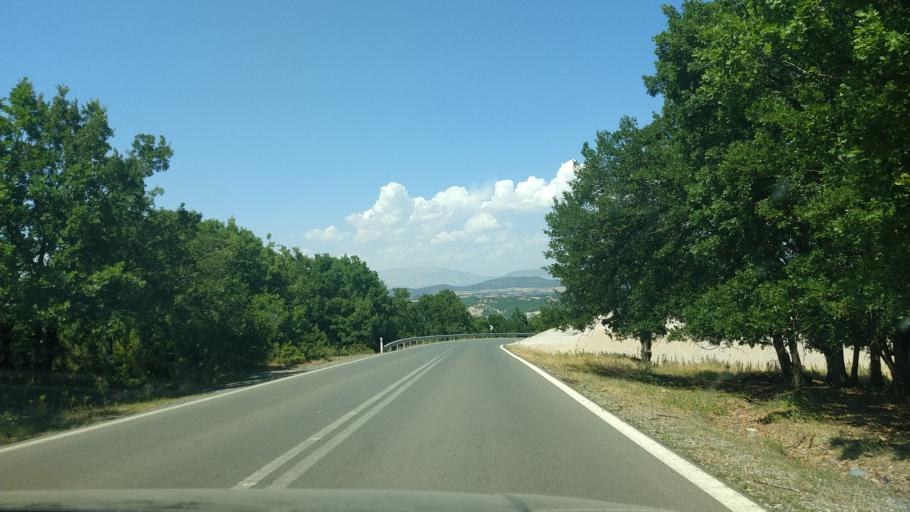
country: GR
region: West Macedonia
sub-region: Nomos Grevenon
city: Grevena
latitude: 40.0327
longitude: 21.4832
